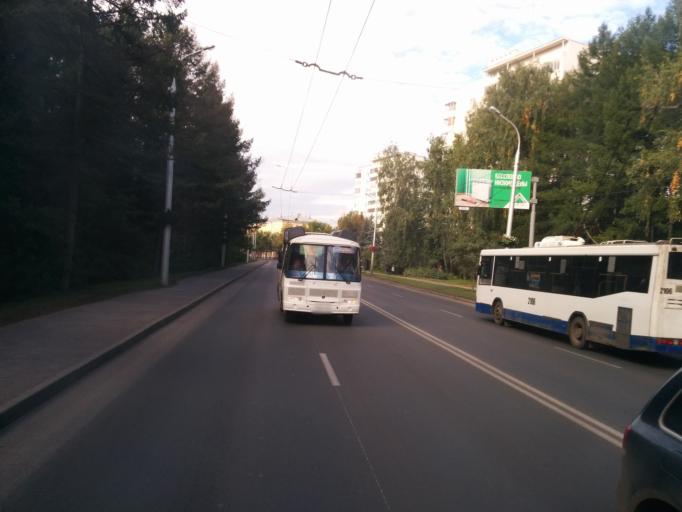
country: RU
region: Bashkortostan
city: Ufa
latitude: 54.8145
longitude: 56.0572
